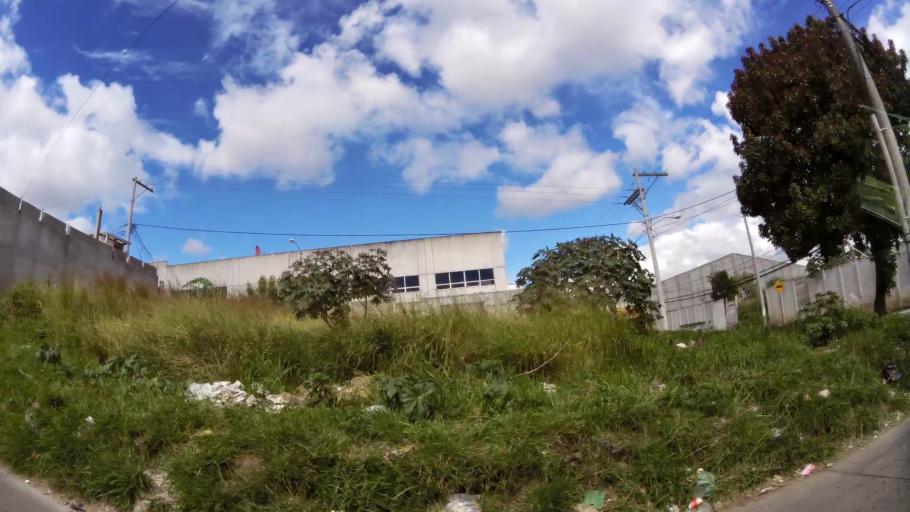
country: GT
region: Guatemala
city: Petapa
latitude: 14.5501
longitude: -90.5438
